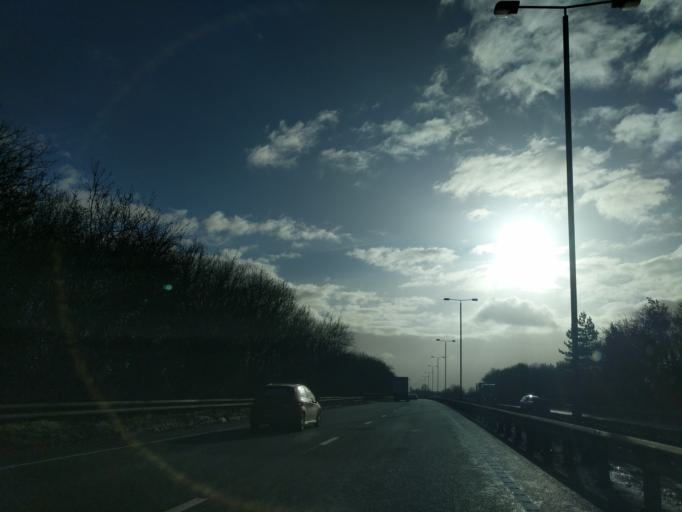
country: GB
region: England
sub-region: Derbyshire
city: Findern
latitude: 52.8974
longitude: -1.5390
